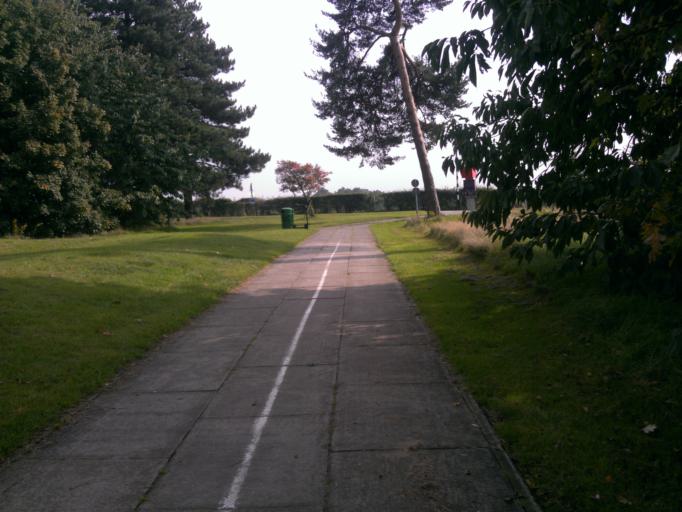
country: GB
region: England
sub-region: Essex
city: Rowhedge
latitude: 51.8744
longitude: 0.9503
